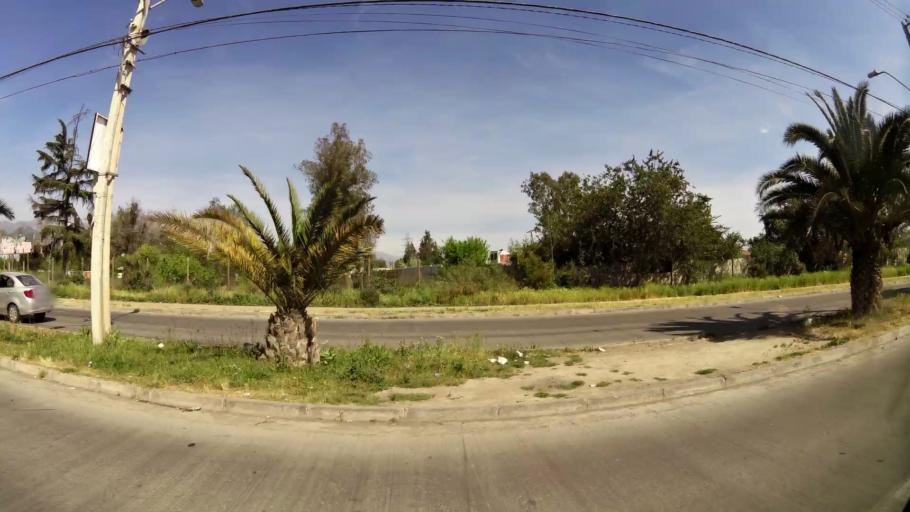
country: CL
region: Santiago Metropolitan
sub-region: Provincia de Cordillera
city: Puente Alto
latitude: -33.5913
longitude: -70.5414
